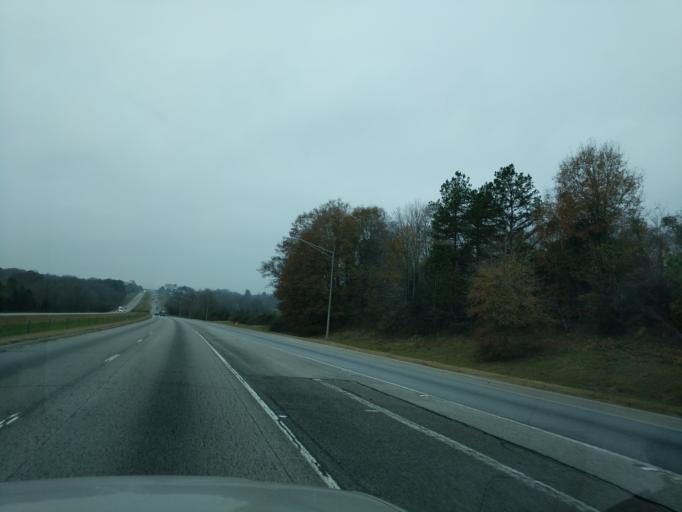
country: US
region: Georgia
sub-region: Franklin County
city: Carnesville
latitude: 34.4144
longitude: -83.1802
